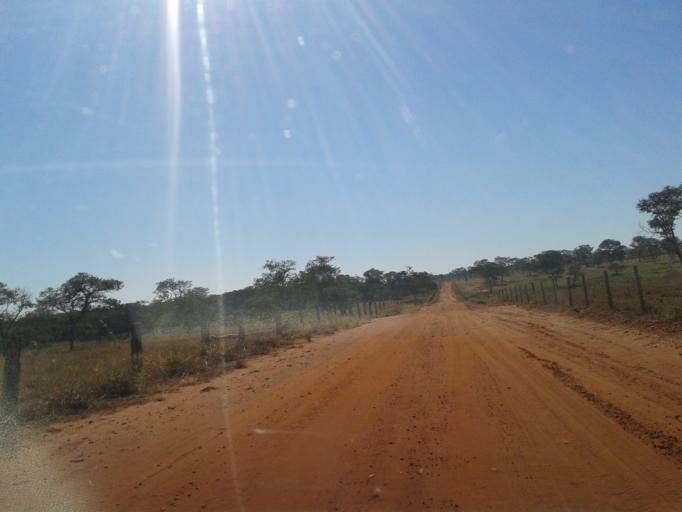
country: BR
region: Minas Gerais
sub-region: Santa Vitoria
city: Santa Vitoria
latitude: -19.0370
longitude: -50.3641
